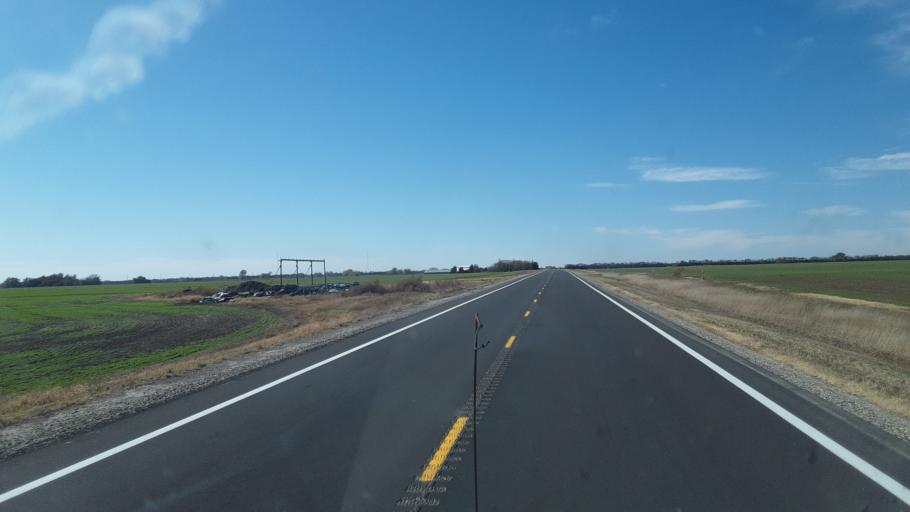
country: US
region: Kansas
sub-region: Rice County
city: Lyons
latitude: 38.3767
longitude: -98.1007
